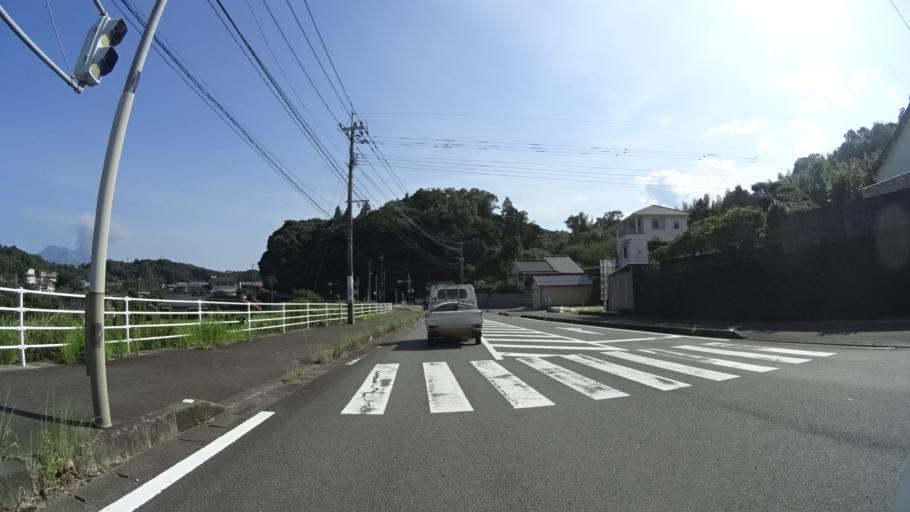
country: JP
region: Kagoshima
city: Kagoshima-shi
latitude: 31.6552
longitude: 130.5504
